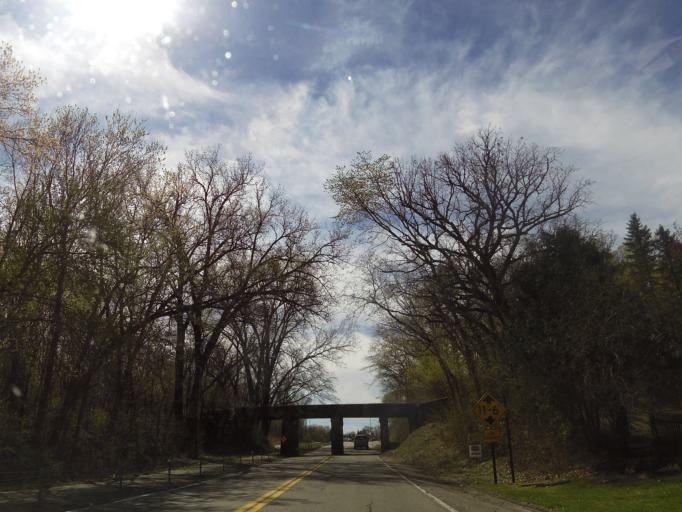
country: US
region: Minnesota
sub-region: Scott County
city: Savage
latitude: 44.7704
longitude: -93.3362
